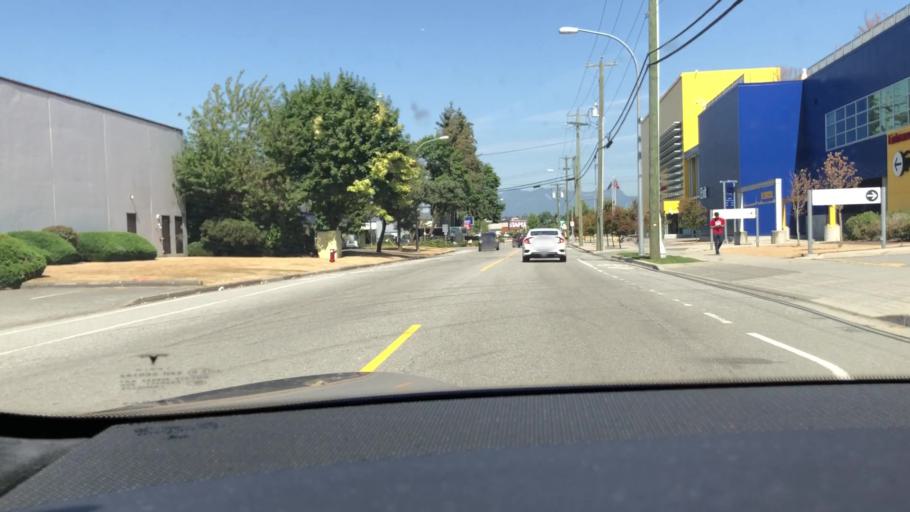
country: CA
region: British Columbia
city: Richmond
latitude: 49.1884
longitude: -123.0803
